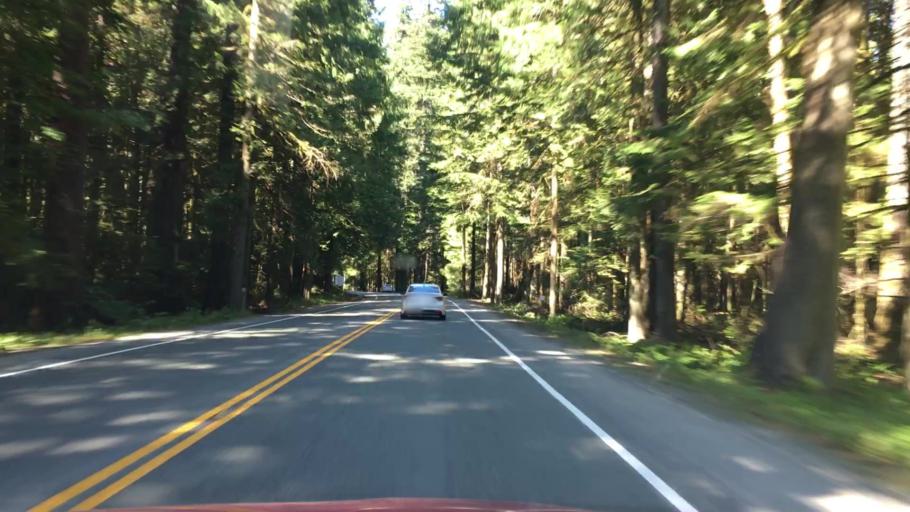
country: CA
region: British Columbia
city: Port Alberni
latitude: 49.2774
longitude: -124.6749
